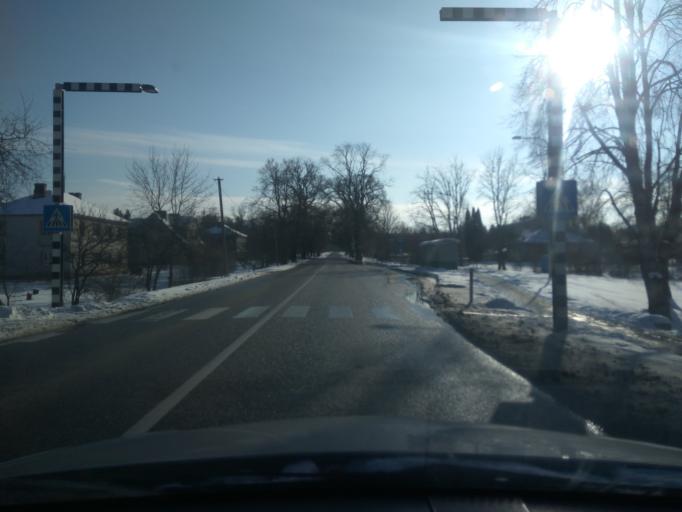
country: LV
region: Kuldigas Rajons
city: Kuldiga
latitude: 57.2789
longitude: 22.0221
